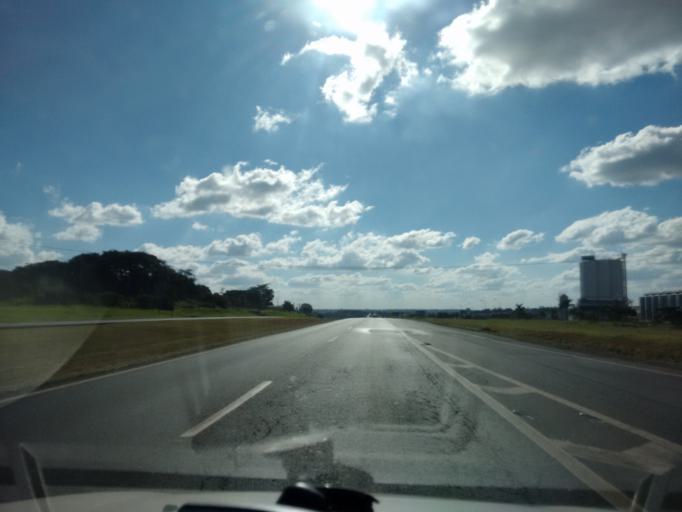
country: BR
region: Sao Paulo
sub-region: Araraquara
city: Araraquara
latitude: -21.8239
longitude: -48.1708
